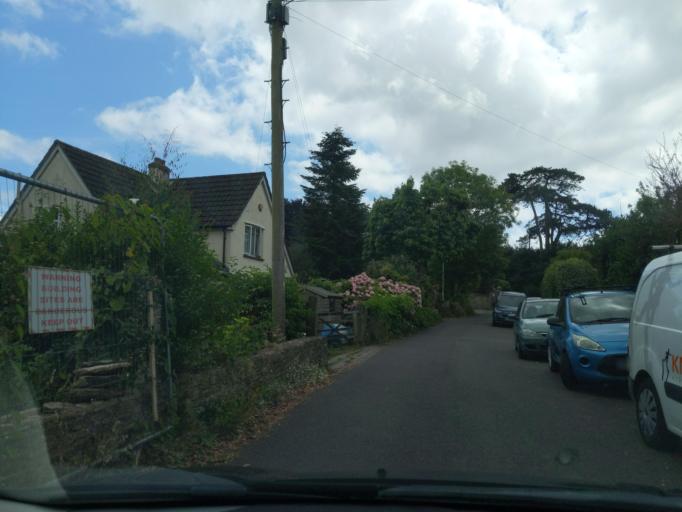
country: GB
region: England
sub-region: Devon
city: Totnes
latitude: 50.4334
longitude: -3.6701
